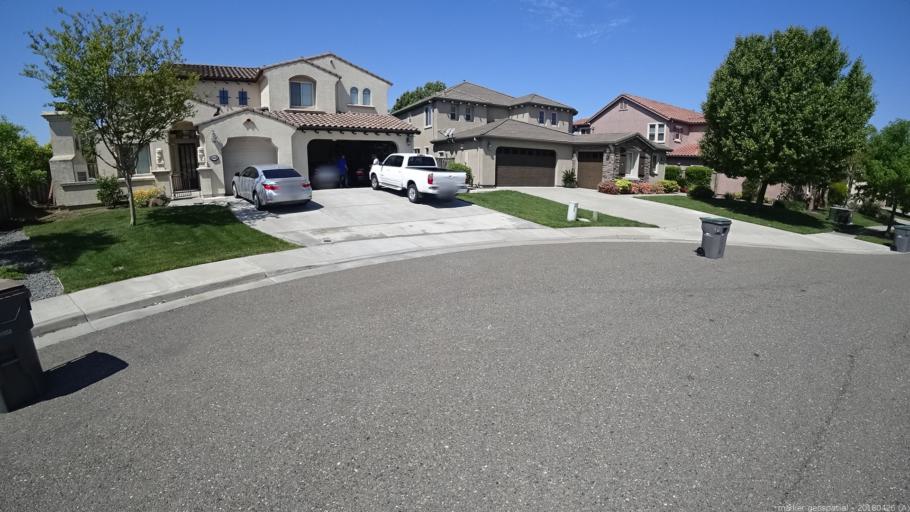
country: US
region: California
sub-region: Yolo County
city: West Sacramento
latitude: 38.5280
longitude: -121.5736
